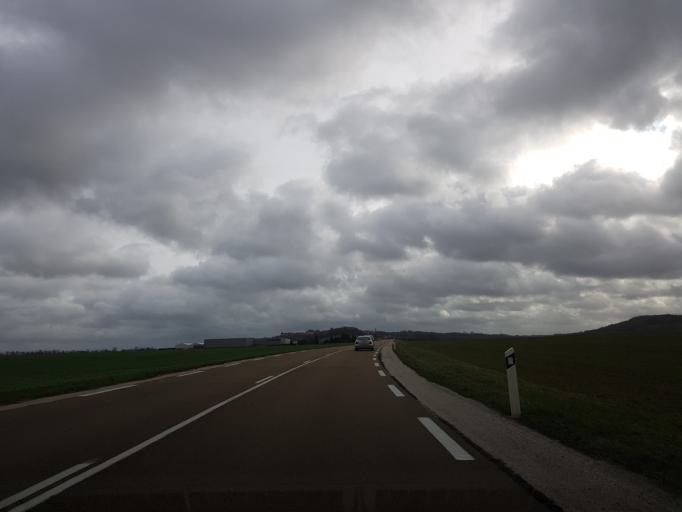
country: FR
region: Champagne-Ardenne
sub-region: Departement de la Haute-Marne
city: Langres
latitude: 47.8944
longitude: 5.3133
